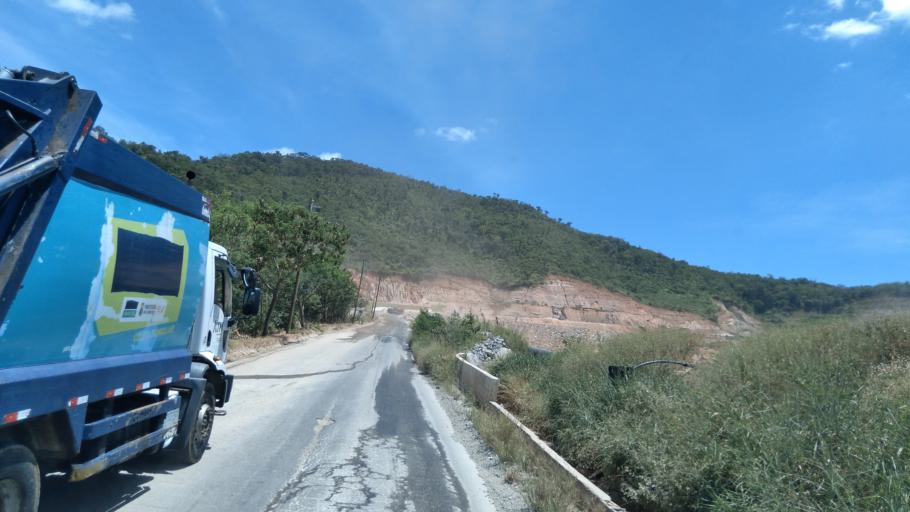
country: BR
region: Minas Gerais
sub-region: Santa Luzia
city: Santa Luzia
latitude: -19.8541
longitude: -43.8498
